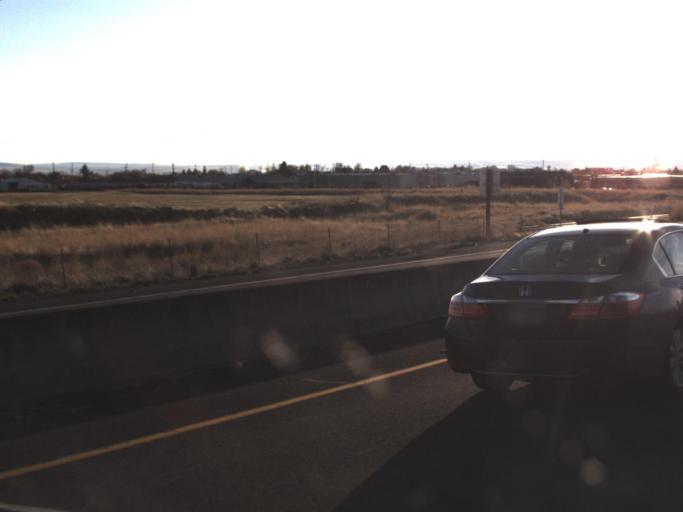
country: US
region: Washington
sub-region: Walla Walla County
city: Walla Walla East
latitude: 46.0823
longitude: -118.2983
